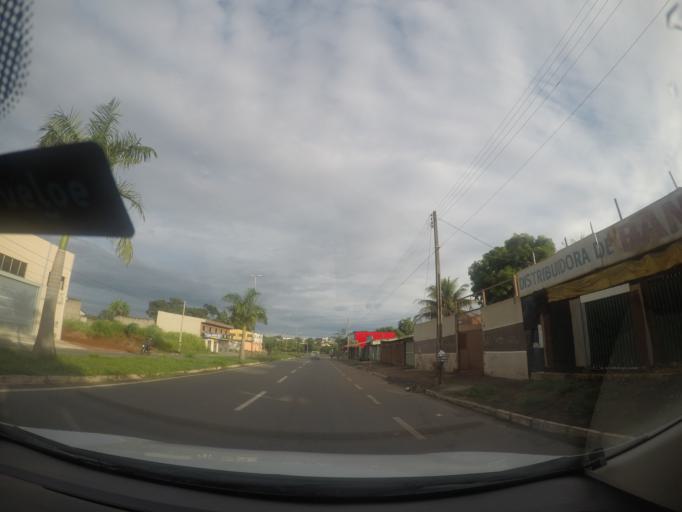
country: BR
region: Goias
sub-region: Goiania
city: Goiania
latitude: -16.6378
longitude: -49.3178
